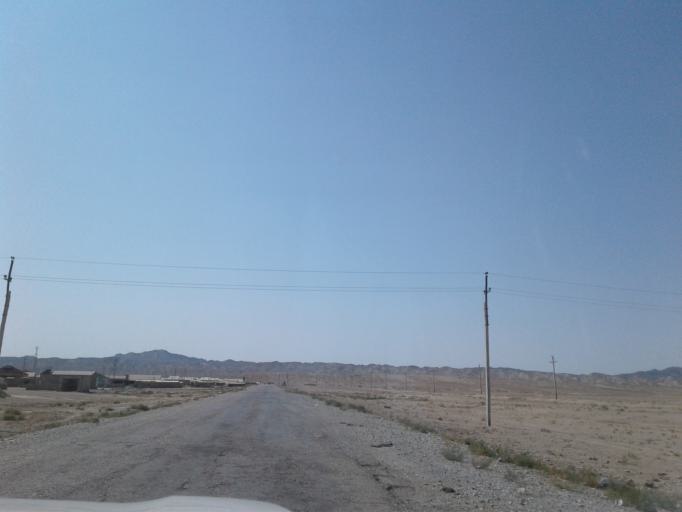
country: TM
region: Balkan
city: Gazanjyk
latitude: 39.1572
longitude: 55.3076
